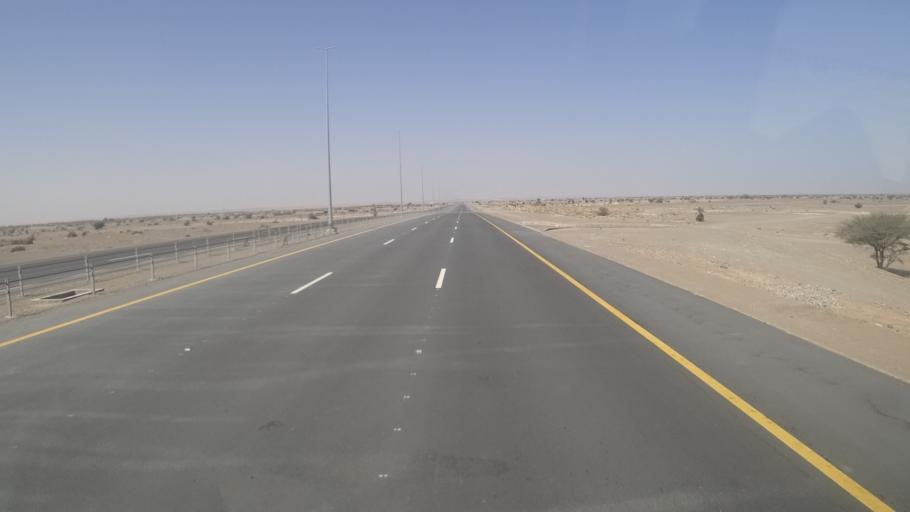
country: OM
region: Ash Sharqiyah
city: Badiyah
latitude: 22.2758
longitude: 59.1986
